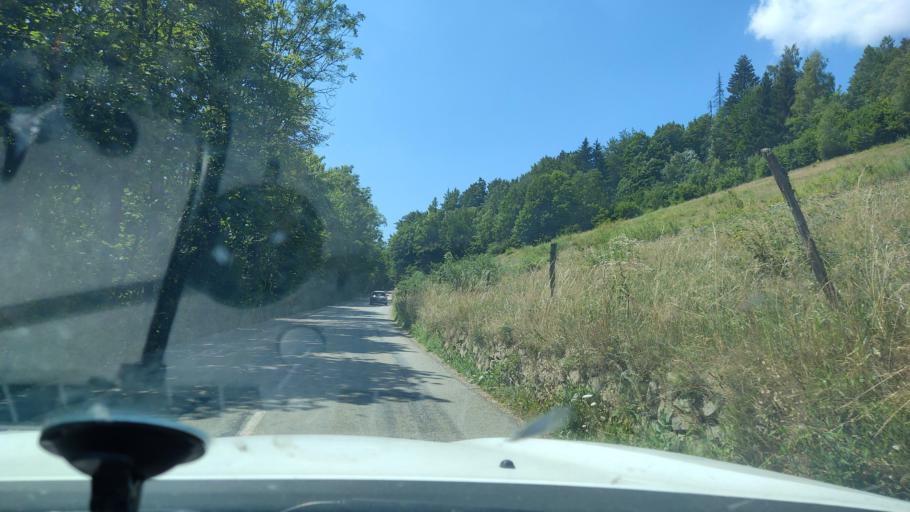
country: FR
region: Rhone-Alpes
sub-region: Departement de la Savoie
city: Mery
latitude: 45.6576
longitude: 6.0313
